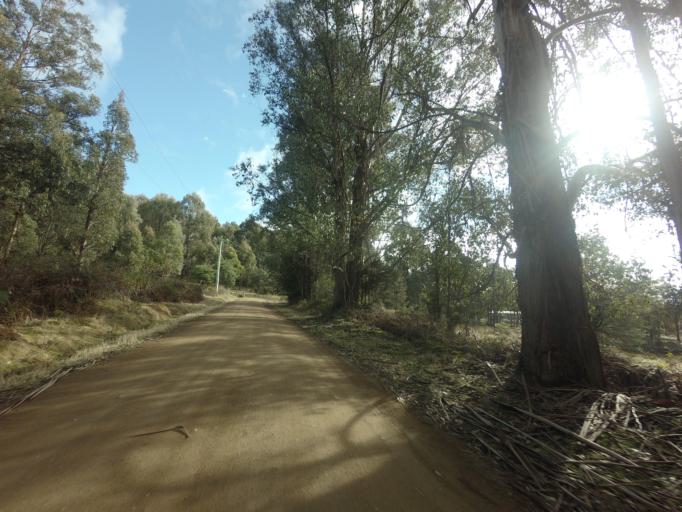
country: AU
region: Tasmania
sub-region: Derwent Valley
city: New Norfolk
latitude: -42.7880
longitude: 146.9182
